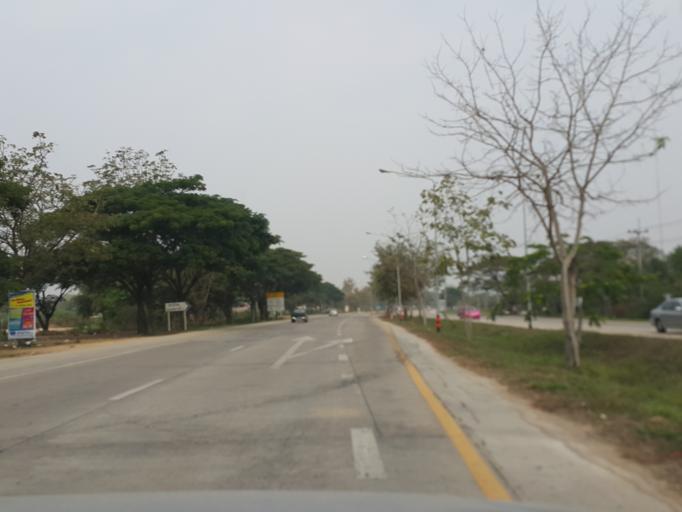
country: TH
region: Lampang
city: Ko Kha
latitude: 18.1942
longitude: 99.4065
